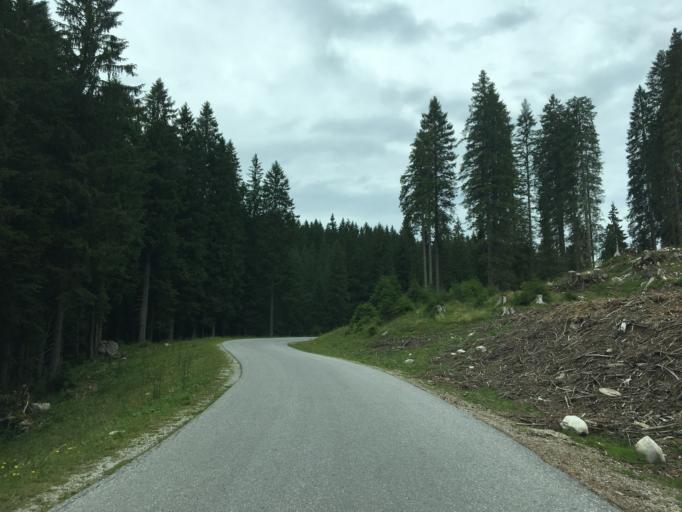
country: AT
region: Salzburg
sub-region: Politischer Bezirk Salzburg-Umgebung
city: Strobl
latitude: 47.6415
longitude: 13.4198
